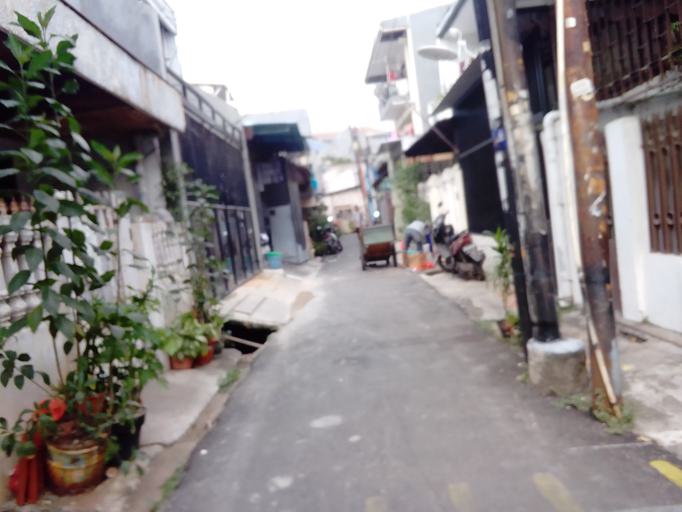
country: ID
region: Jakarta Raya
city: Jakarta
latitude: -6.1616
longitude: 106.8139
